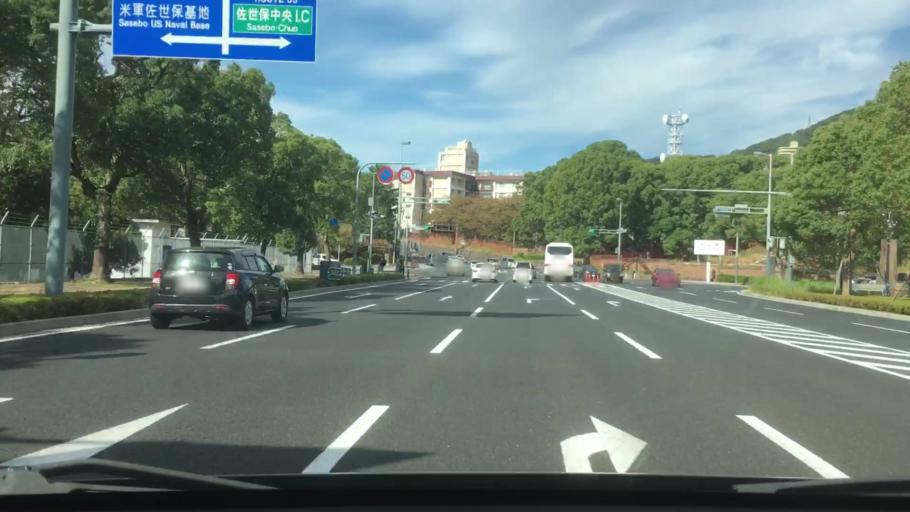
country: JP
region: Nagasaki
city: Sasebo
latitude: 33.1689
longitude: 129.7153
